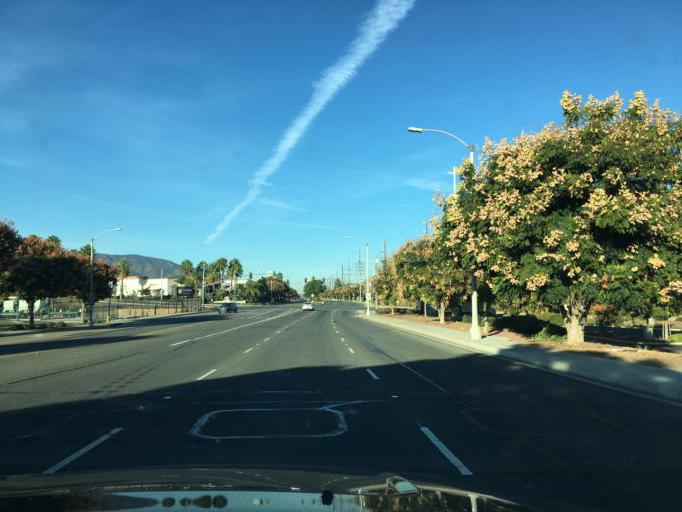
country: US
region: California
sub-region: Riverside County
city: Corona
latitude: 33.8547
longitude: -117.5598
